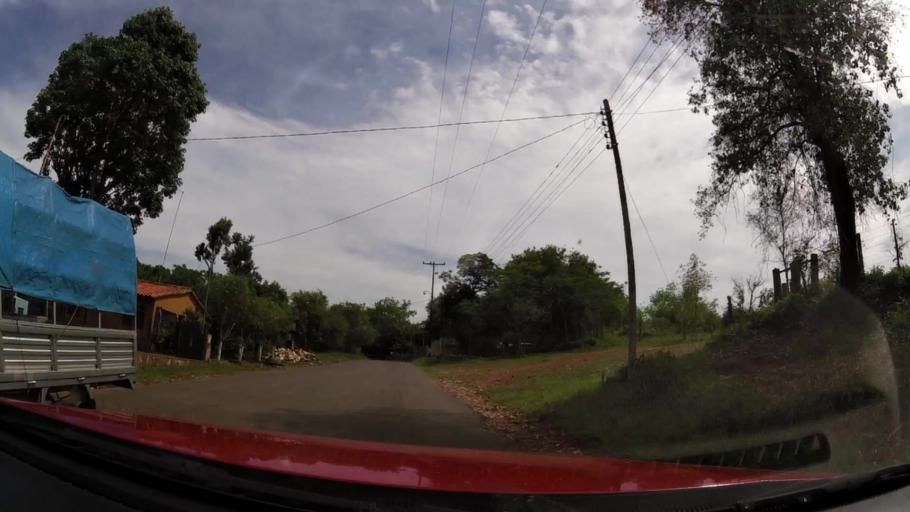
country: PY
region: Central
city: Limpio
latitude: -25.1732
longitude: -57.4423
